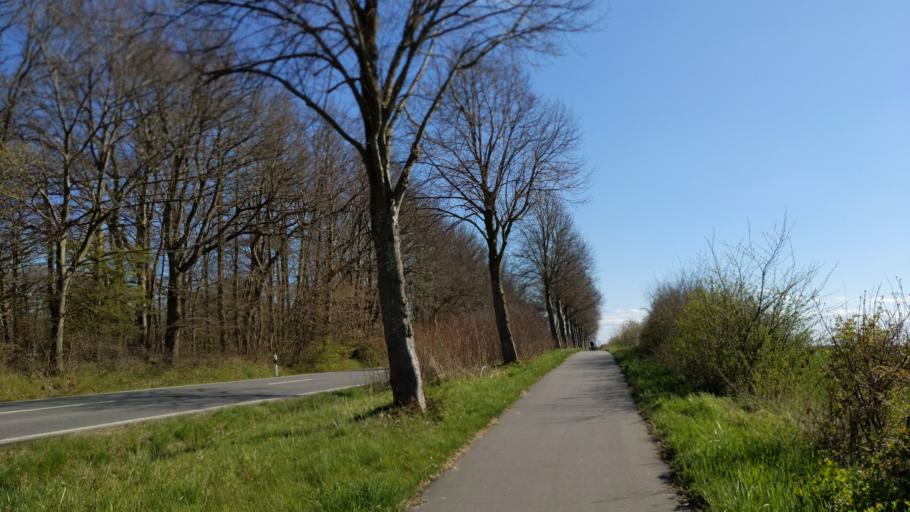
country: DE
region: Schleswig-Holstein
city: Eutin
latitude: 54.1133
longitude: 10.6110
